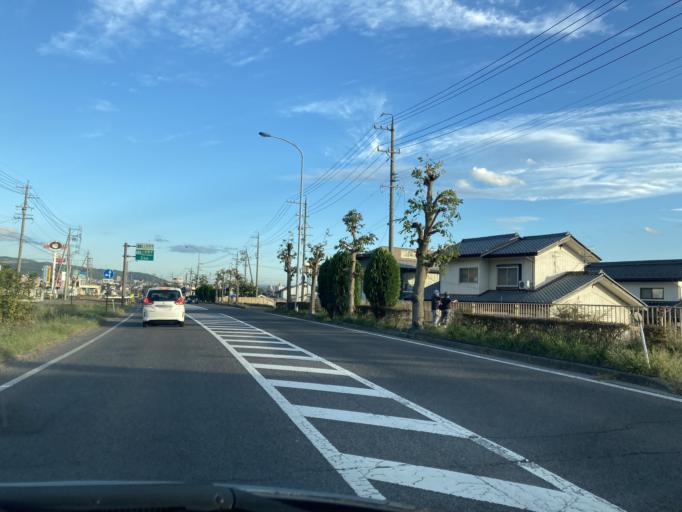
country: JP
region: Nagano
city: Ueda
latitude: 36.4117
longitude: 138.2621
